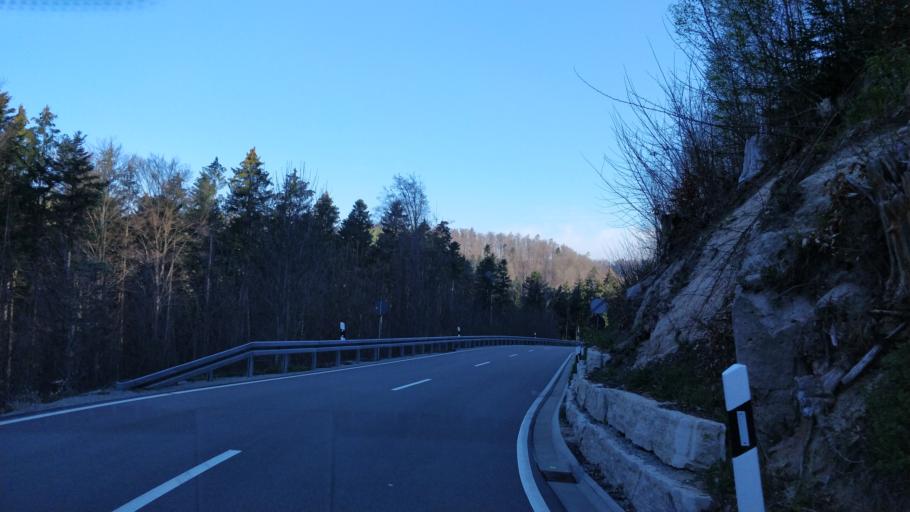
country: DE
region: Baden-Wuerttemberg
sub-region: Regierungsbezirk Stuttgart
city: Oberrot
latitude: 49.0392
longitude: 9.6966
